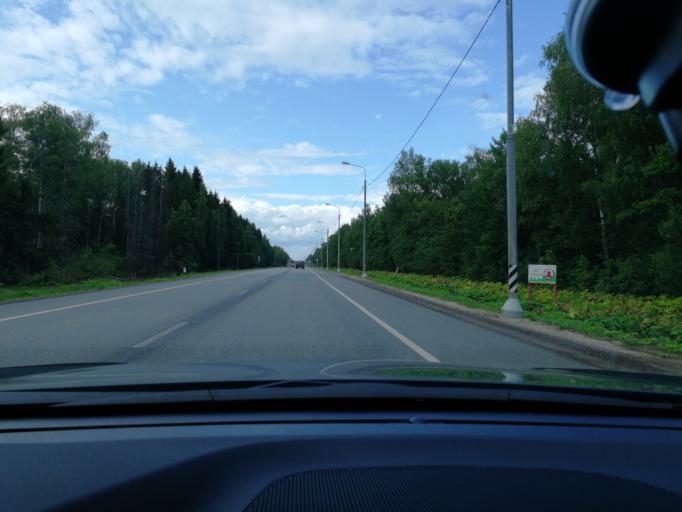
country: RU
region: Moskovskaya
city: Proletarskiy
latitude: 55.0535
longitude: 37.4334
